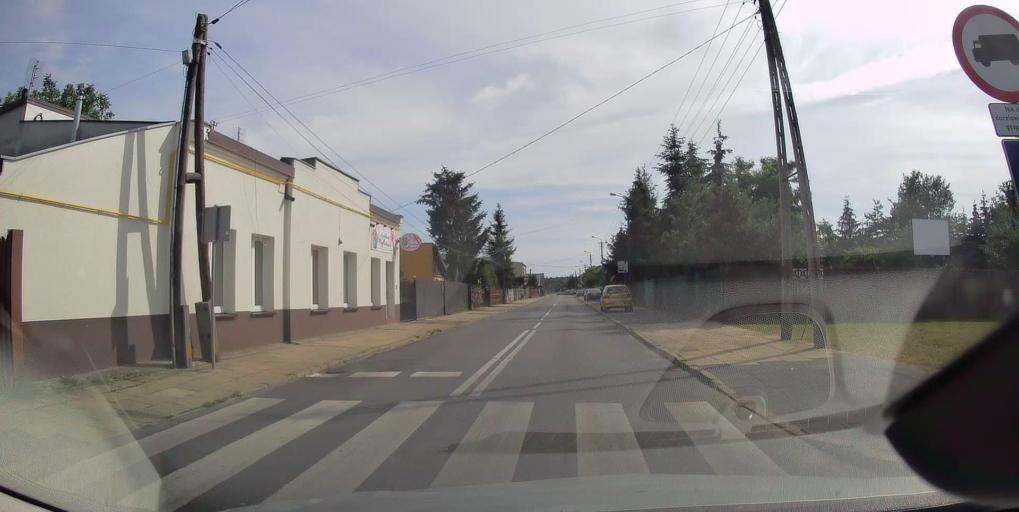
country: PL
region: Lodz Voivodeship
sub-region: Powiat tomaszowski
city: Tomaszow Mazowiecki
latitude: 51.5247
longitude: 19.9976
